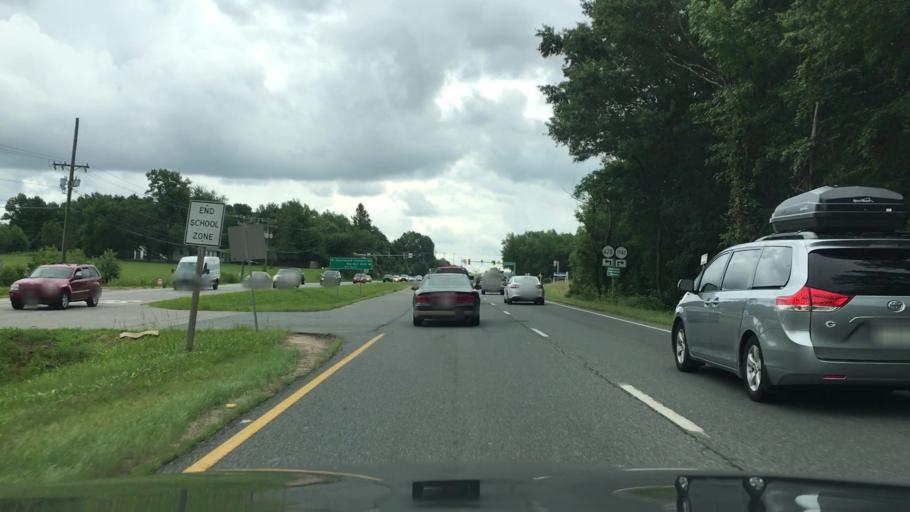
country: US
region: Virginia
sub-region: Spotsylvania County
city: Spotsylvania
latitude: 38.2925
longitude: -77.5792
